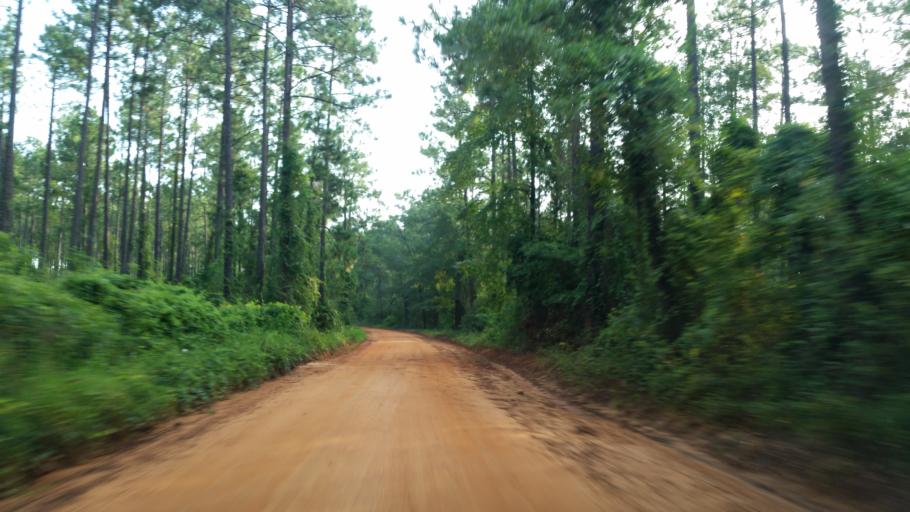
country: US
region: Alabama
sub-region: Escambia County
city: Atmore
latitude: 30.9185
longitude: -87.5771
